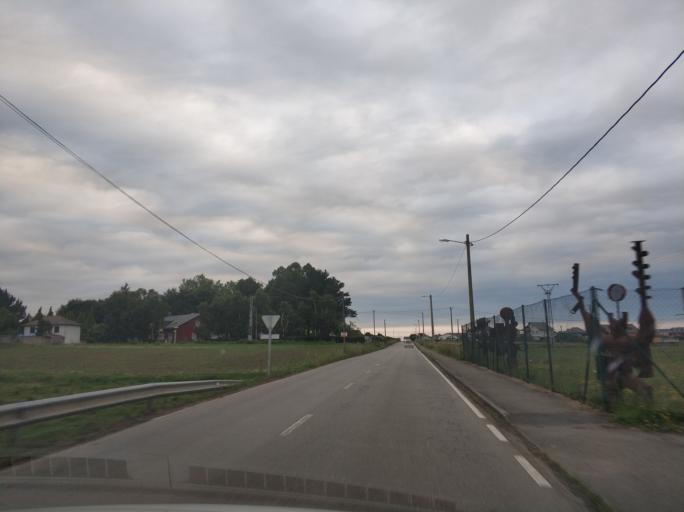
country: ES
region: Asturias
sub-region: Province of Asturias
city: Navia
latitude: 43.5360
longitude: -6.5200
